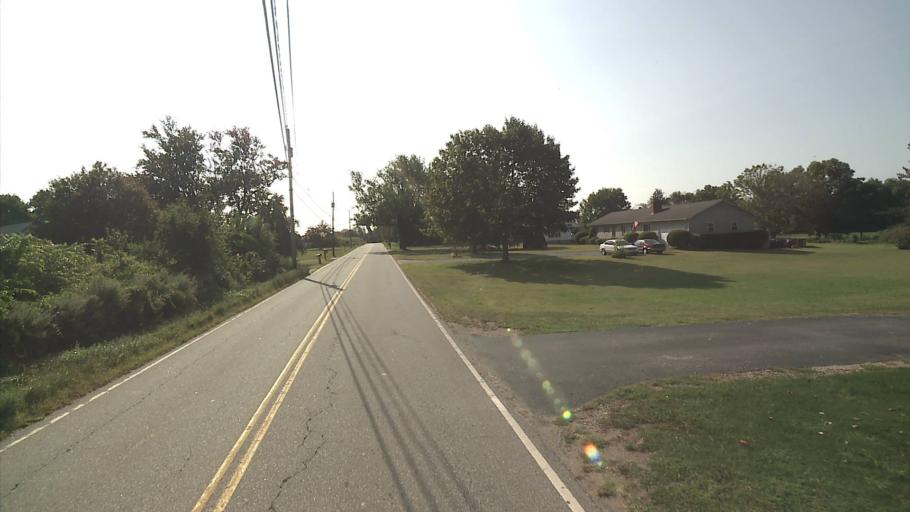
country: US
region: Connecticut
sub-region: Windham County
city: South Windham
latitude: 41.6099
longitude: -72.1772
